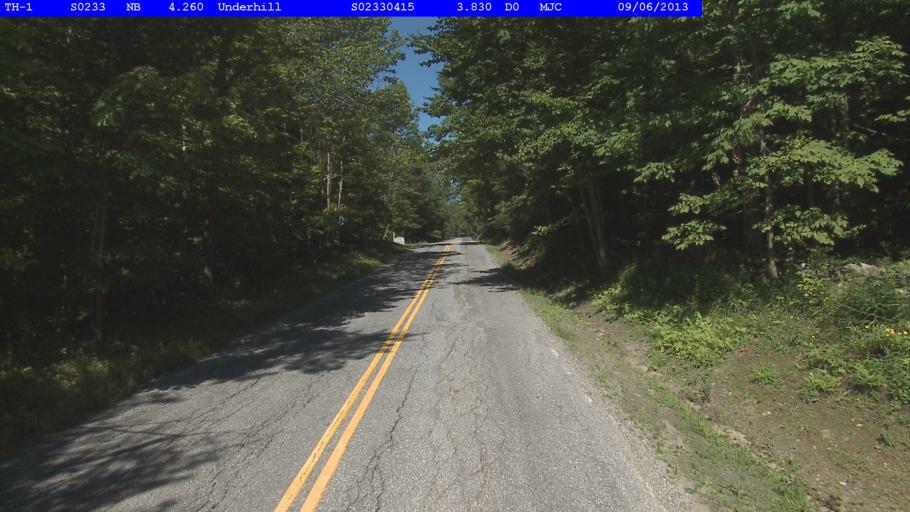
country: US
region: Vermont
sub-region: Chittenden County
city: Jericho
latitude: 44.5223
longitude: -72.8811
